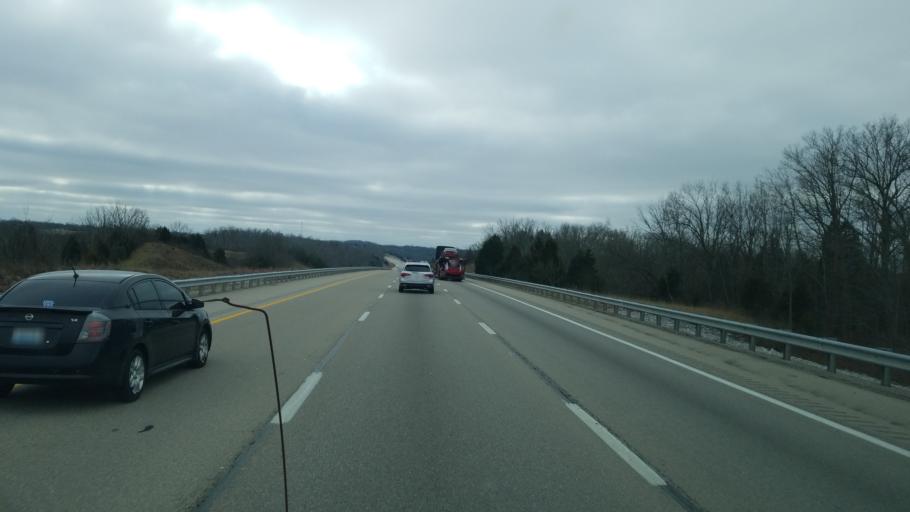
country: US
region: Kentucky
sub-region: Grant County
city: Williamstown
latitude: 38.5200
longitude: -84.5879
